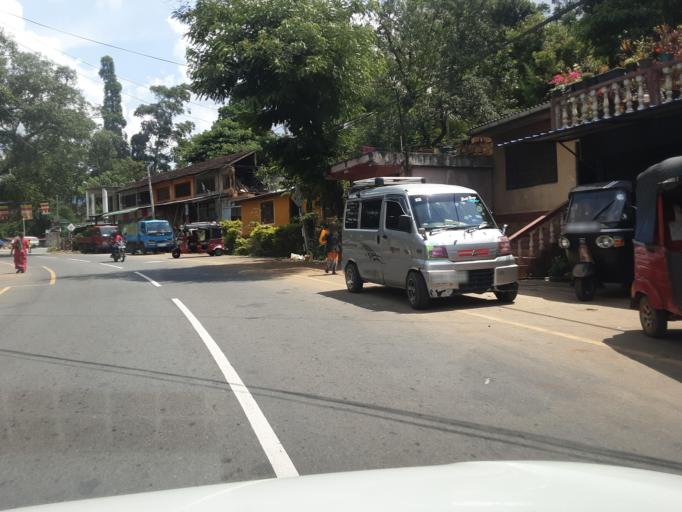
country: LK
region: Central
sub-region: Nuwara Eliya District
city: Nuwara Eliya
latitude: 6.9226
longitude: 80.9001
